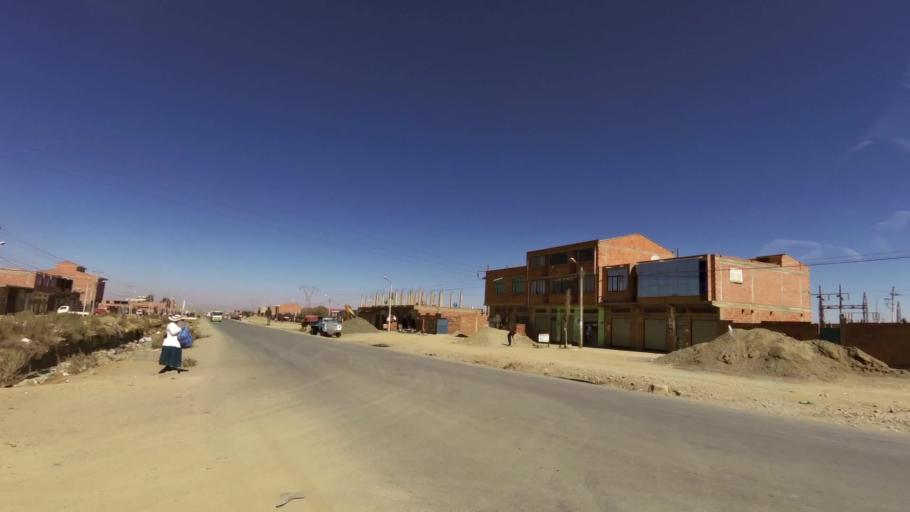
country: BO
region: La Paz
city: La Paz
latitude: -16.5698
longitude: -68.2235
